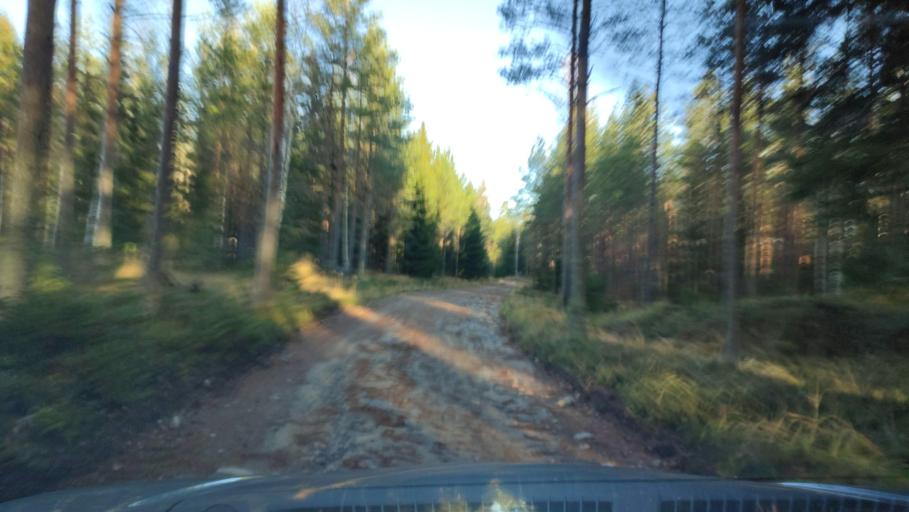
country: FI
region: Southern Ostrobothnia
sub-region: Suupohja
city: Karijoki
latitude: 62.2142
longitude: 21.6277
